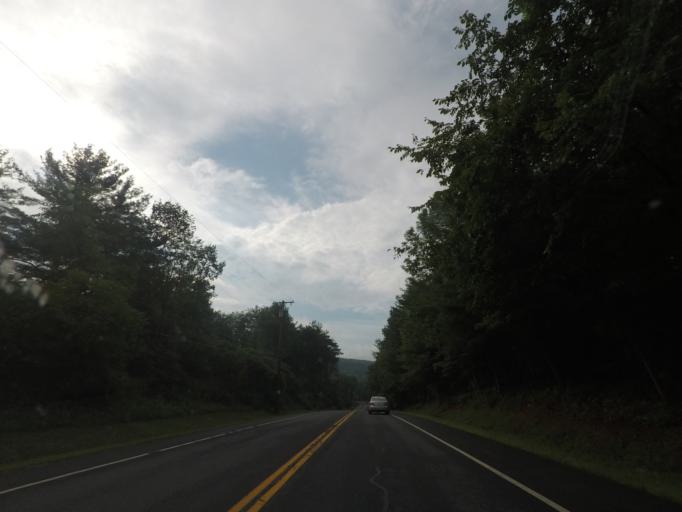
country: US
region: New York
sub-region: Rensselaer County
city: Nassau
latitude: 42.4991
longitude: -73.5556
